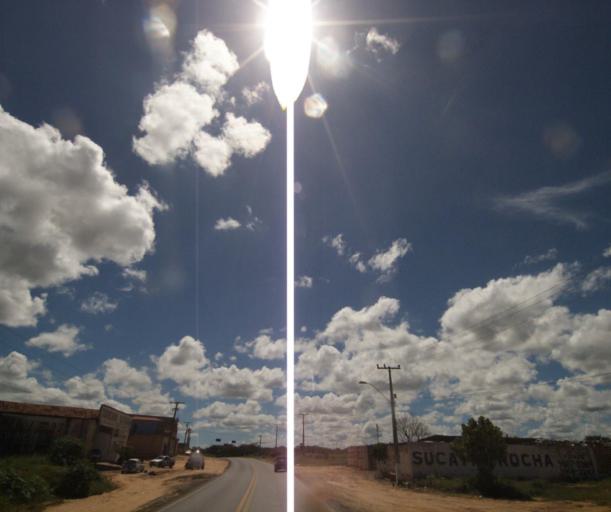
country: BR
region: Bahia
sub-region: Sao Felix Do Coribe
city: Santa Maria da Vitoria
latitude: -13.4084
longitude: -44.1861
